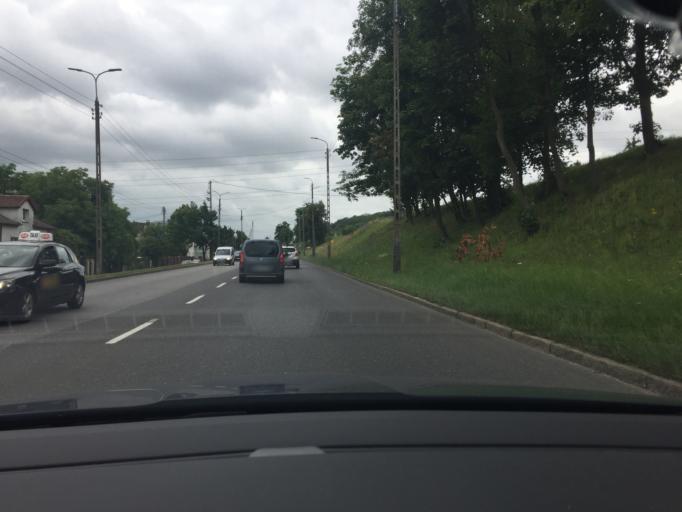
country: PL
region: Pomeranian Voivodeship
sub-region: Powiat gdanski
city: Pruszcz Gdanski
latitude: 54.2952
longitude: 18.6341
